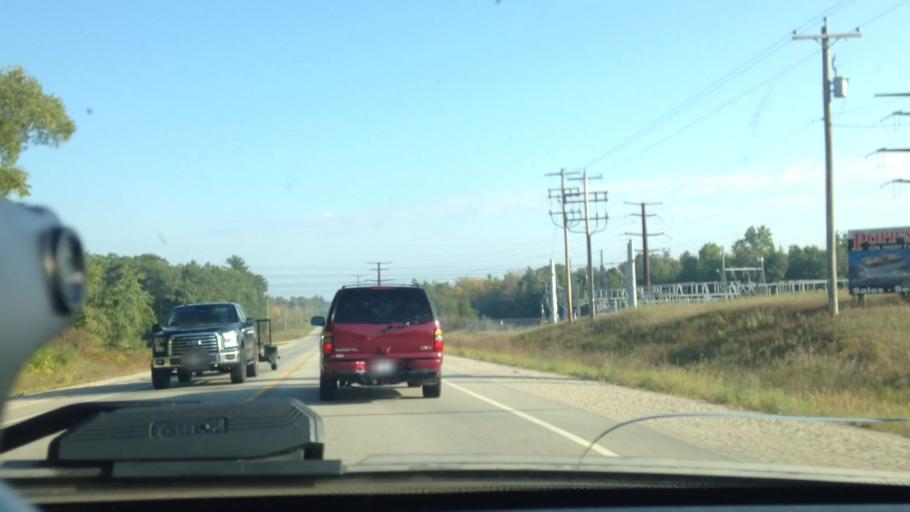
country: US
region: Wisconsin
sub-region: Marinette County
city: Peshtigo
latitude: 45.1753
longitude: -87.9959
